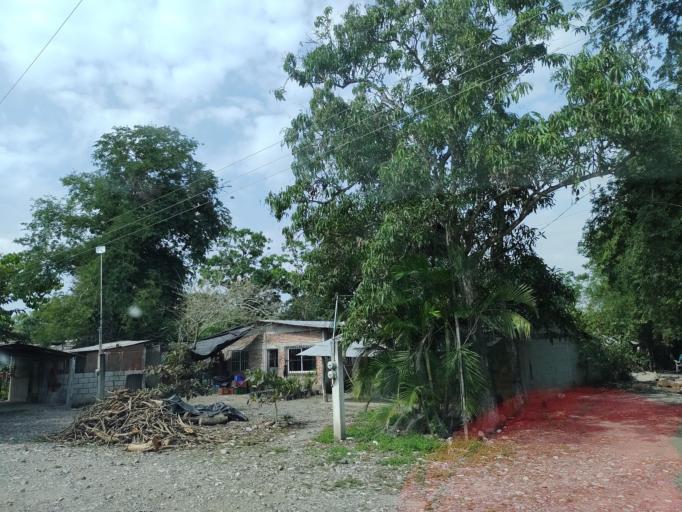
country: MX
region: Puebla
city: Espinal
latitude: 20.2731
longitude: -97.3331
